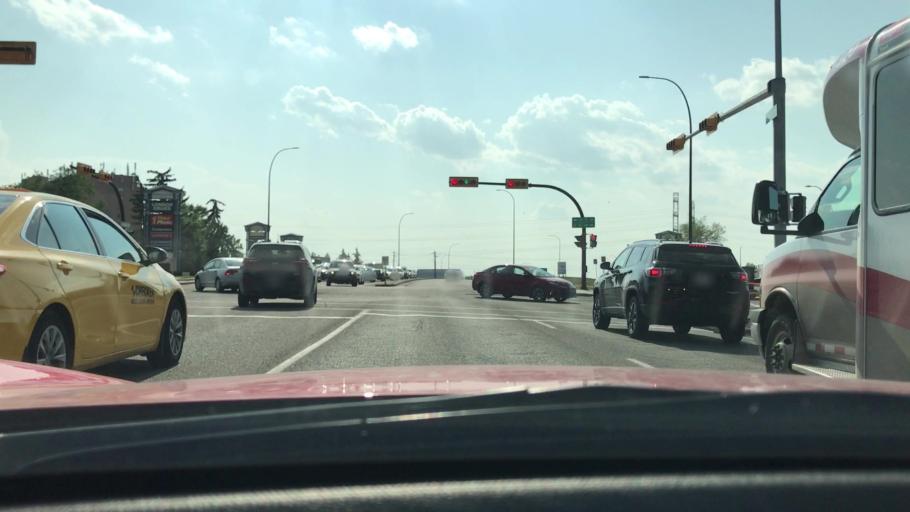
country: CA
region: Alberta
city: Calgary
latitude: 51.0181
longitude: -114.1593
